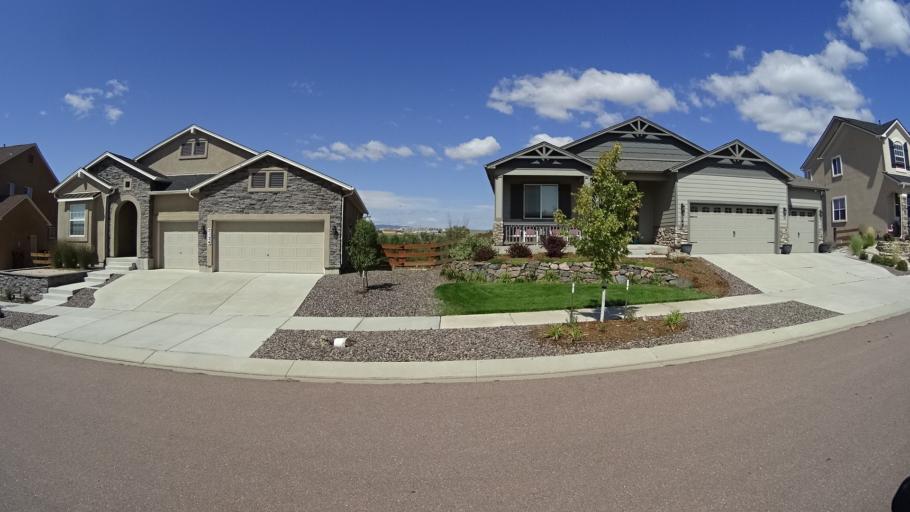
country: US
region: Colorado
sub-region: El Paso County
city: Cimarron Hills
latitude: 38.9343
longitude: -104.6856
